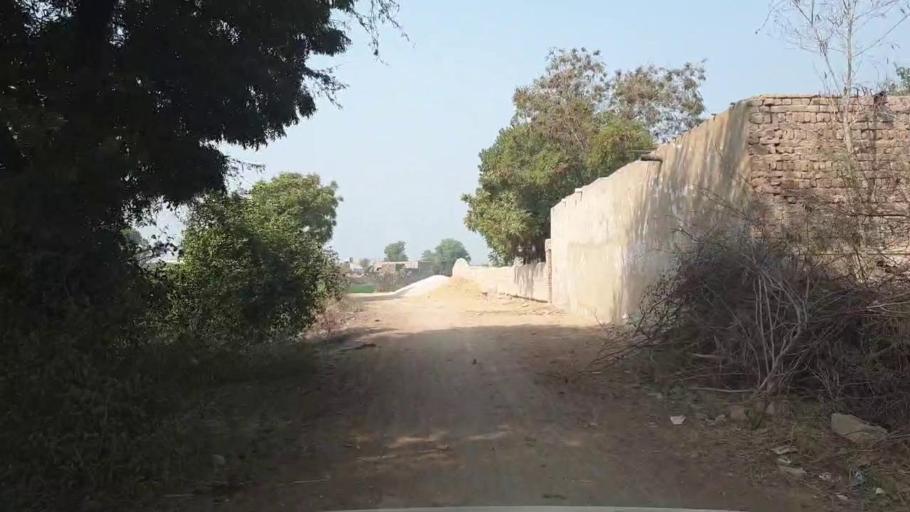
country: PK
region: Sindh
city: Hala
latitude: 25.8222
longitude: 68.4042
